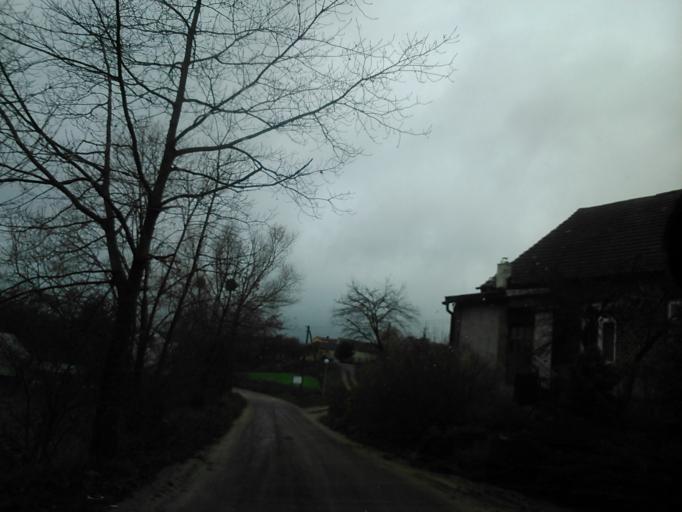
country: PL
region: Kujawsko-Pomorskie
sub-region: Powiat golubsko-dobrzynski
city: Radomin
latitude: 53.1246
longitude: 19.1717
